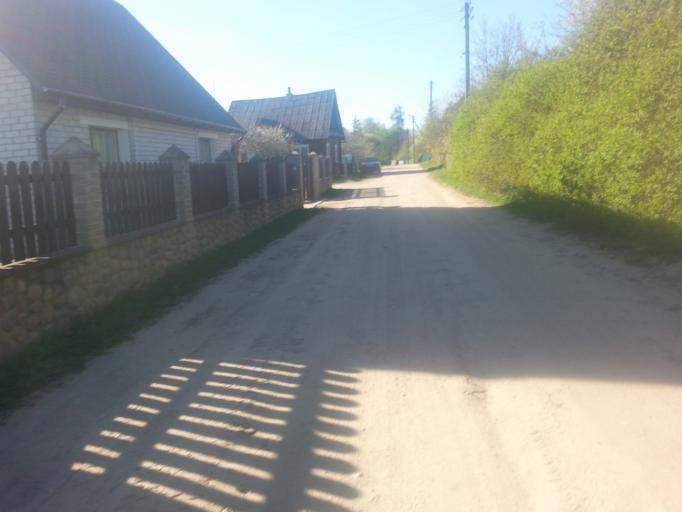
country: BY
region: Minsk
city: Narach
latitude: 54.9336
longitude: 26.6816
